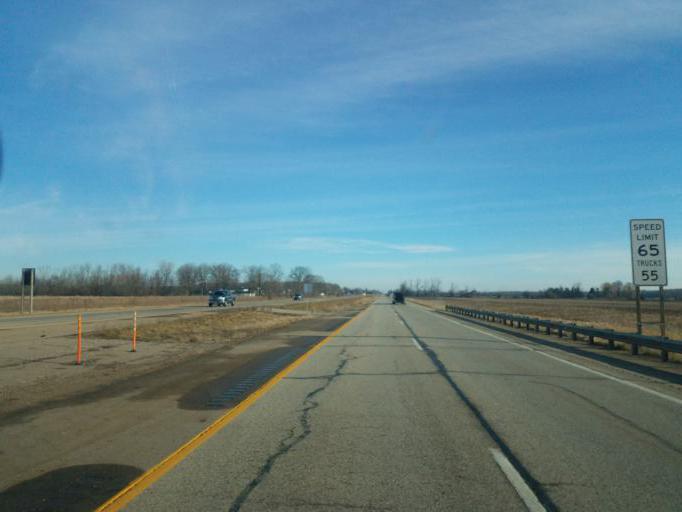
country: US
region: Michigan
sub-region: Gratiot County
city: Ithaca
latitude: 43.1844
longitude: -84.5633
